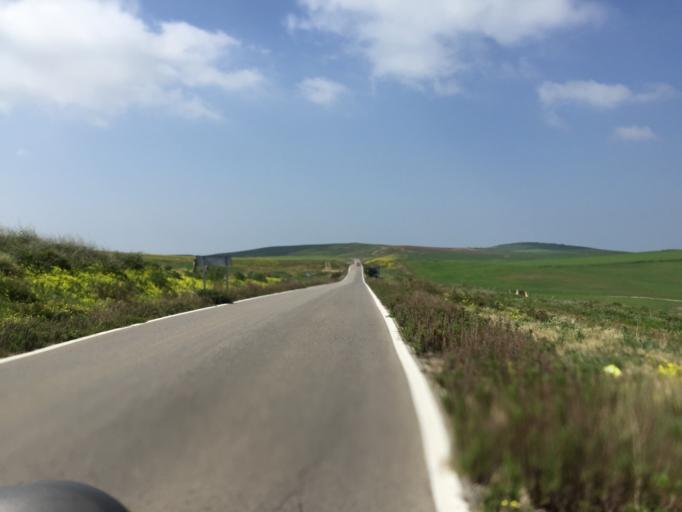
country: ES
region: Andalusia
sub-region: Provincia de Cadiz
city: Vejer de la Frontera
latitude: 36.2364
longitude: -6.0187
